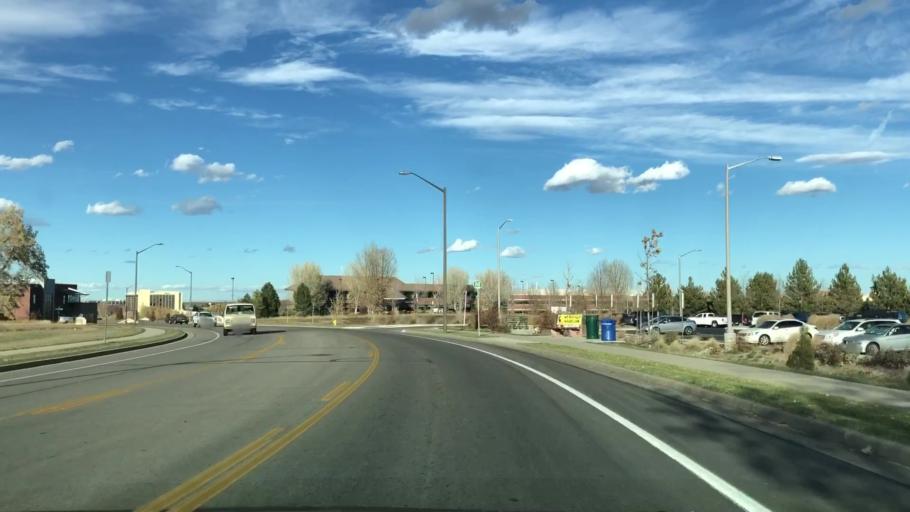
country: US
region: Colorado
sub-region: Larimer County
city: Fort Collins
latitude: 40.5573
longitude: -105.0879
